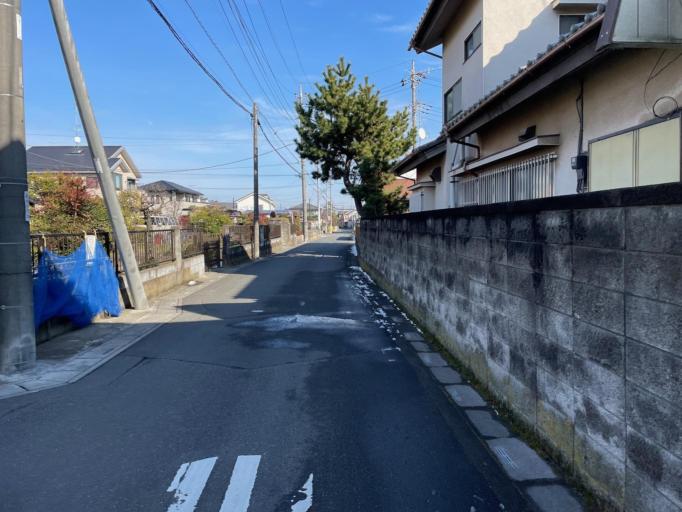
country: JP
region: Saitama
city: Yashio-shi
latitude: 35.8507
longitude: 139.8451
